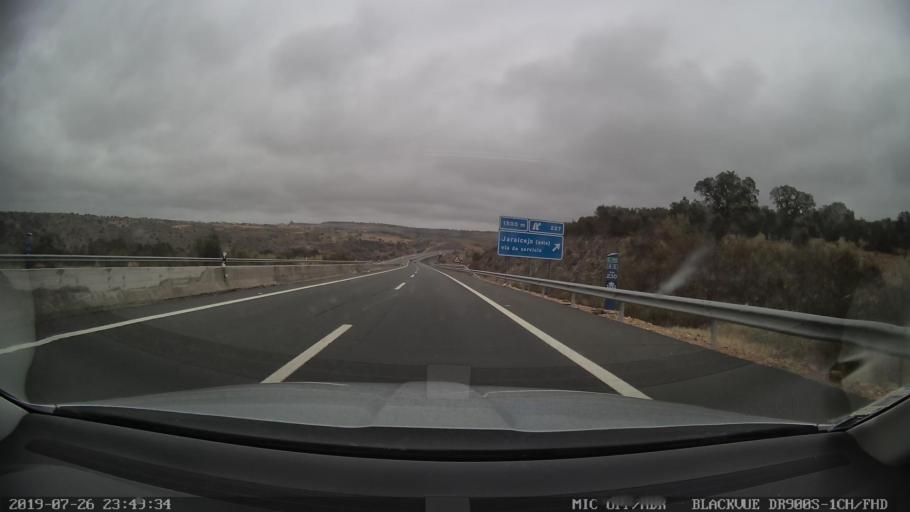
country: ES
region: Extremadura
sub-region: Provincia de Caceres
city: Jaraicejo
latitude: 39.6441
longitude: -5.8081
